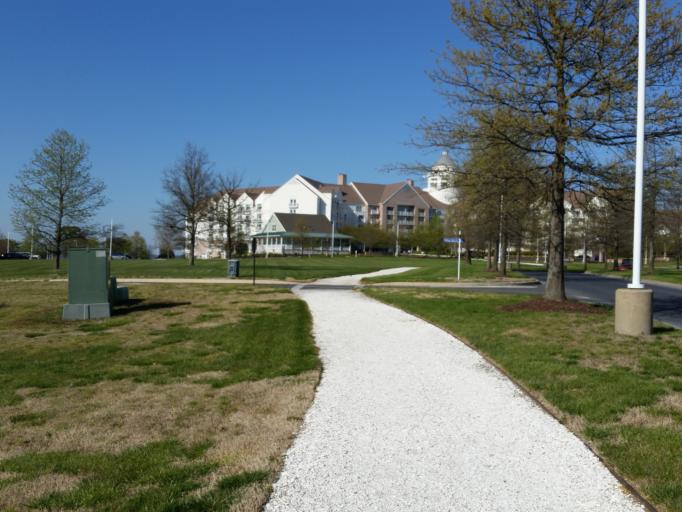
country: US
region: Maryland
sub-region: Dorchester County
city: Cambridge
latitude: 38.5602
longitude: -76.0500
